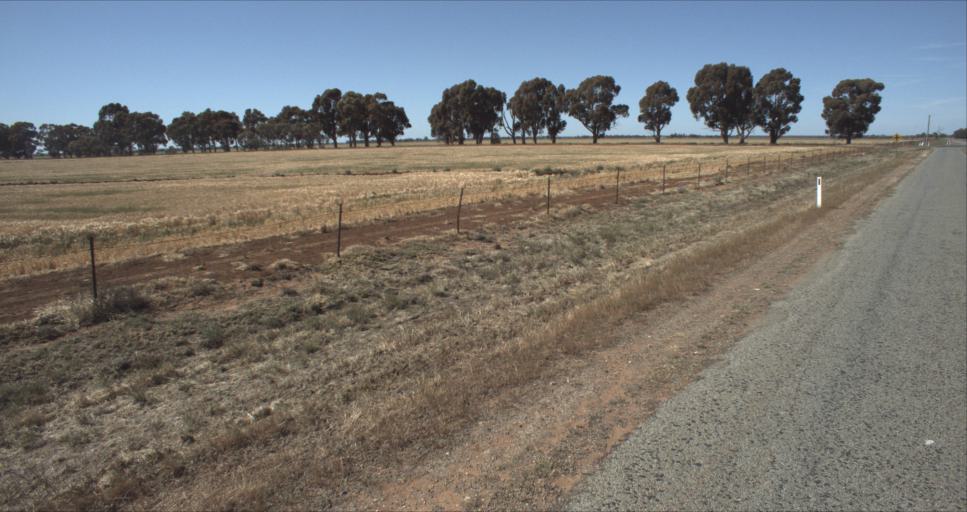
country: AU
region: New South Wales
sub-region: Leeton
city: Leeton
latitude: -34.5483
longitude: 146.3151
